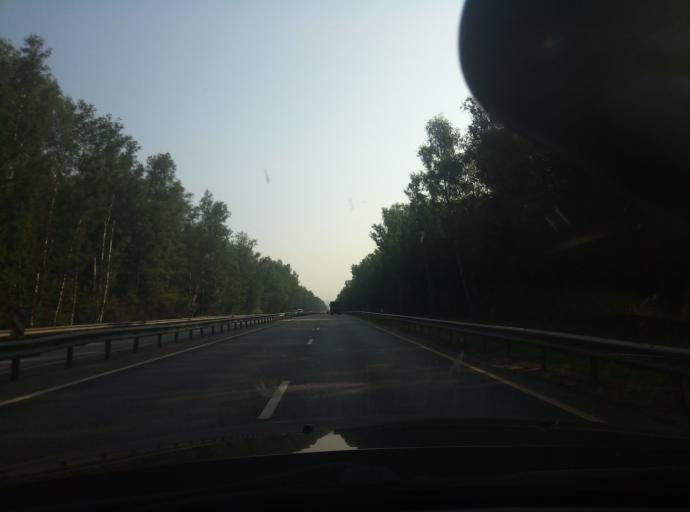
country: RU
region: Kaluga
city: Maloyaroslavets
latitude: 55.0131
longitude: 36.5491
